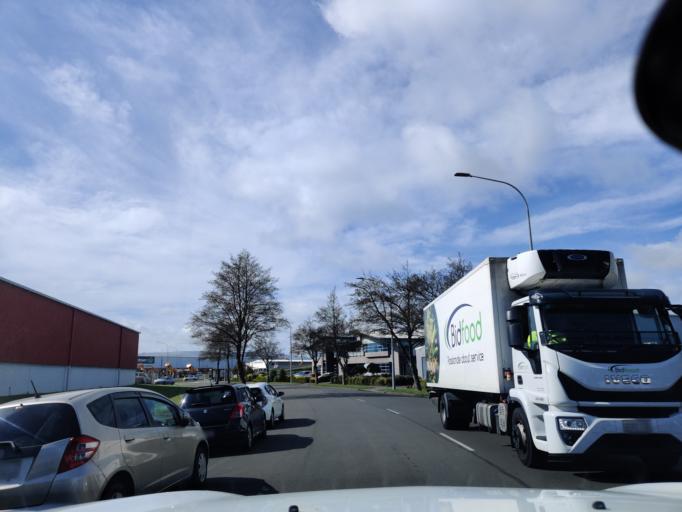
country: NZ
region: Manawatu-Wanganui
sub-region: Palmerston North City
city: Palmerston North
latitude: -40.3352
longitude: 175.6424
